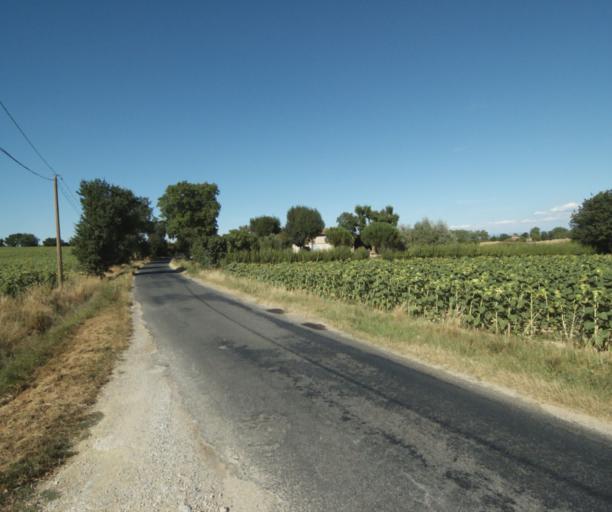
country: FR
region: Midi-Pyrenees
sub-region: Departement de la Haute-Garonne
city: Revel
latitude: 43.5002
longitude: 1.9453
